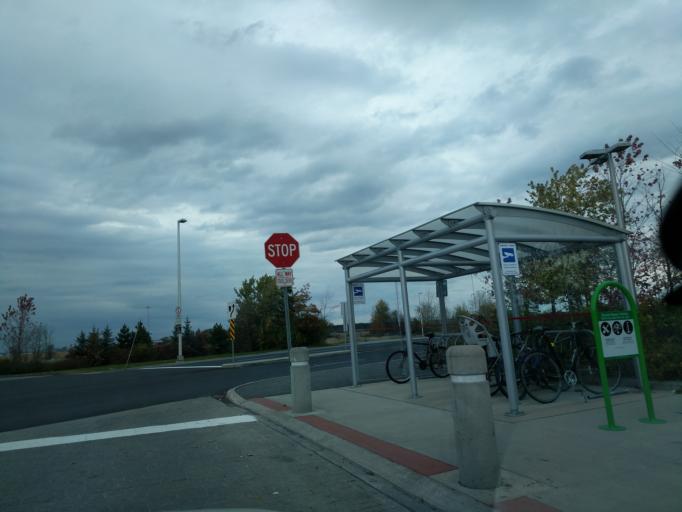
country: CA
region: Ontario
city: Bells Corners
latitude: 45.2989
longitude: -75.7357
